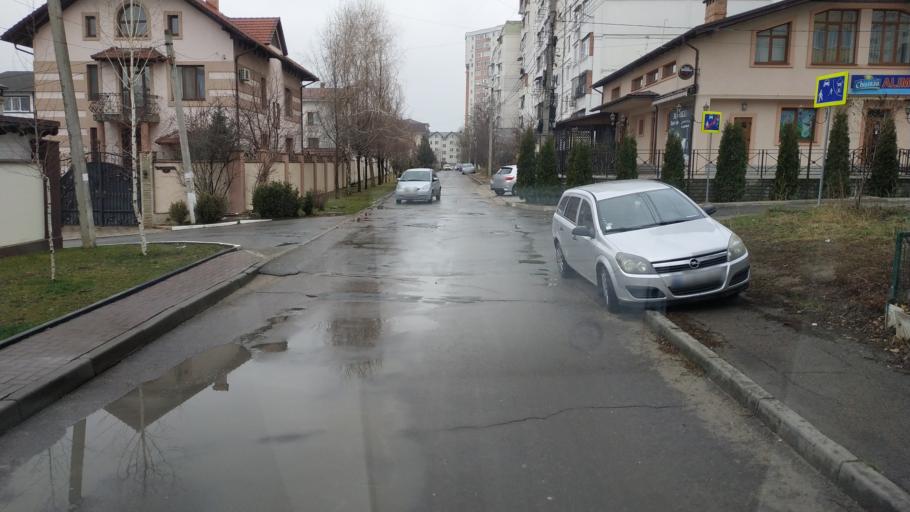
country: MD
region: Chisinau
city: Vatra
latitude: 47.0399
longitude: 28.7619
